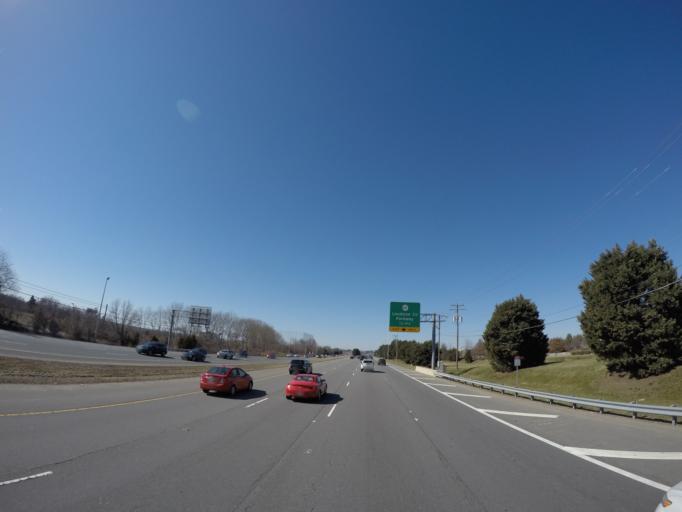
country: US
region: Virginia
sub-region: Loudoun County
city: University Center
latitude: 39.0500
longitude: -77.4373
